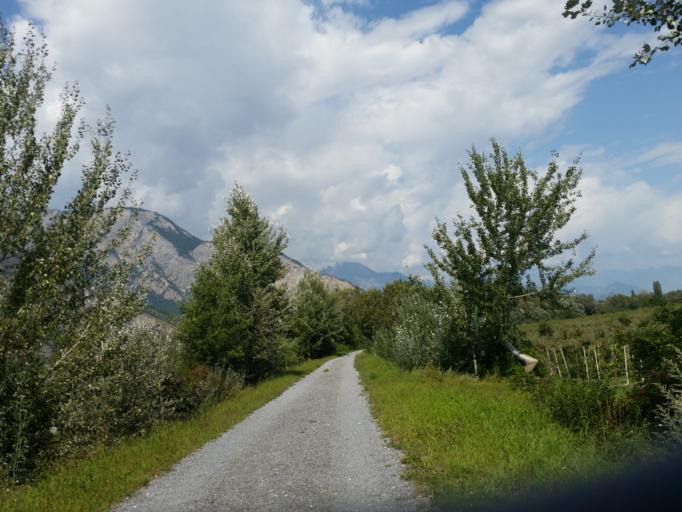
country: CH
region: Valais
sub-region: Martigny District
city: Leytron
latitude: 46.1740
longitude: 7.2018
